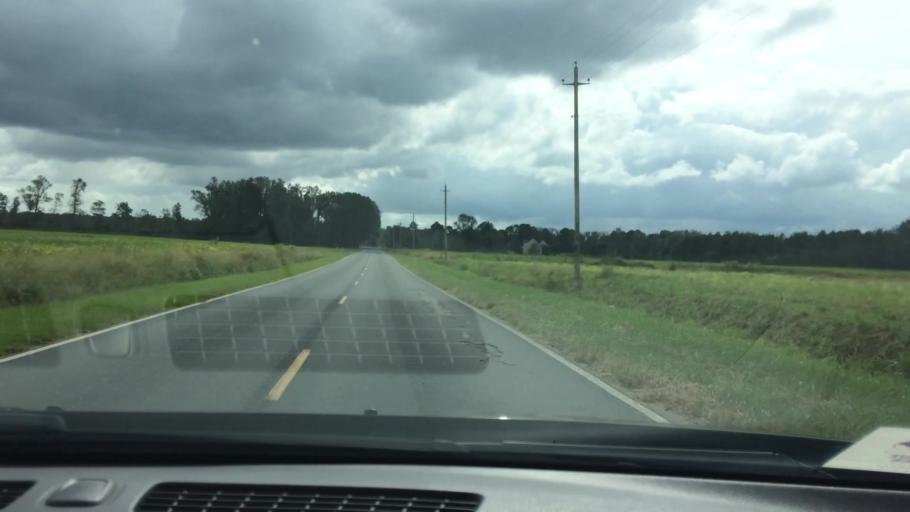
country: US
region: North Carolina
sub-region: Pitt County
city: Farmville
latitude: 35.5436
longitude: -77.5450
